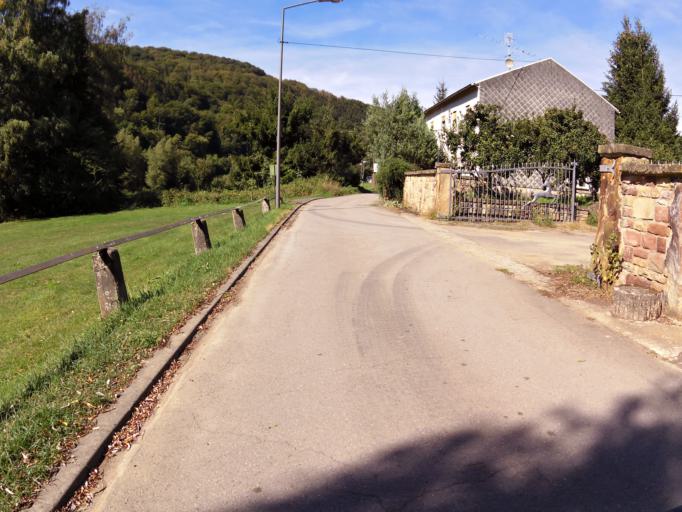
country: LU
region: Grevenmacher
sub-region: Canton d'Echternach
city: Rosport
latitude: 49.7868
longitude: 6.5095
